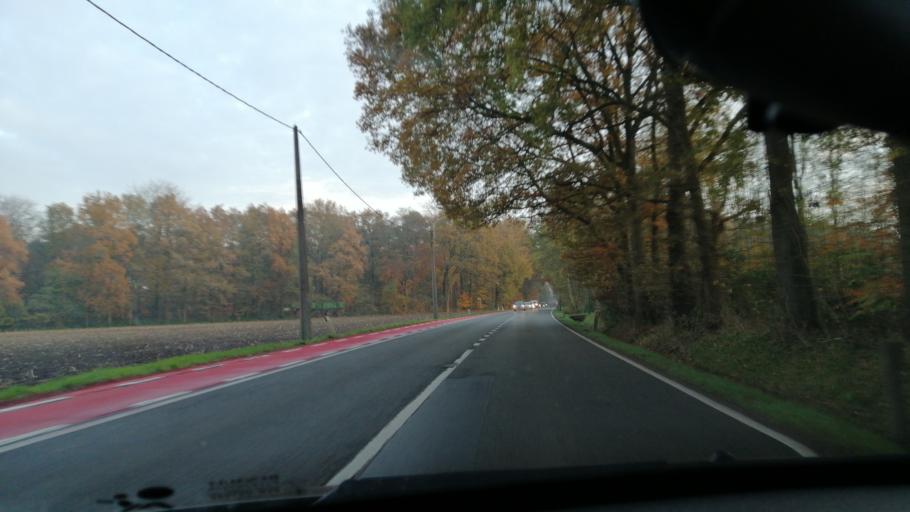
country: BE
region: Flanders
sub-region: Provincie Antwerpen
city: Oostmalle
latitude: 51.2921
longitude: 4.7458
